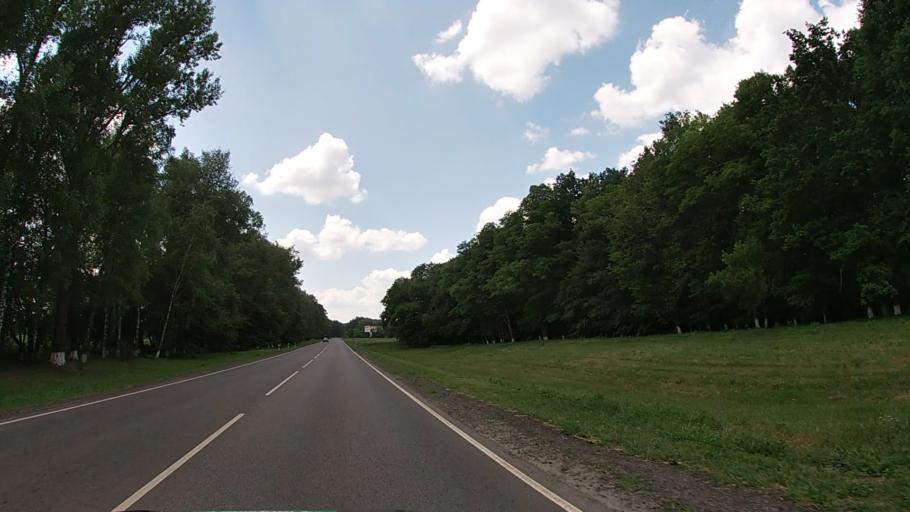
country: RU
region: Belgorod
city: Grayvoron
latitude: 50.4983
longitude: 35.7183
